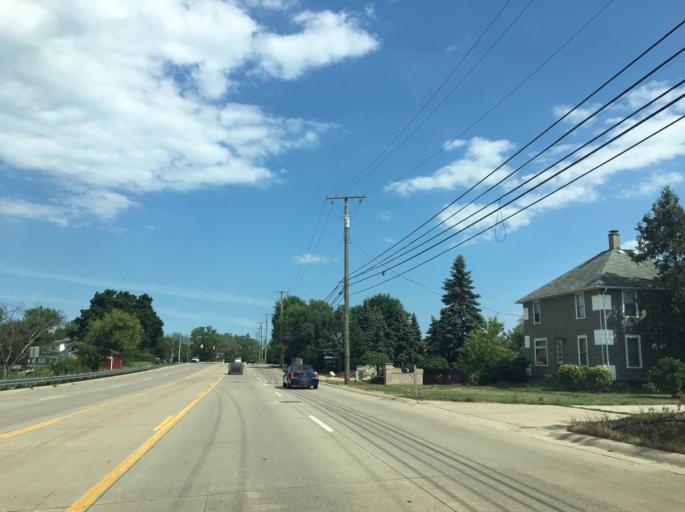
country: US
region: Michigan
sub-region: Macomb County
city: Clinton
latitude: 42.6063
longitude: -82.9199
